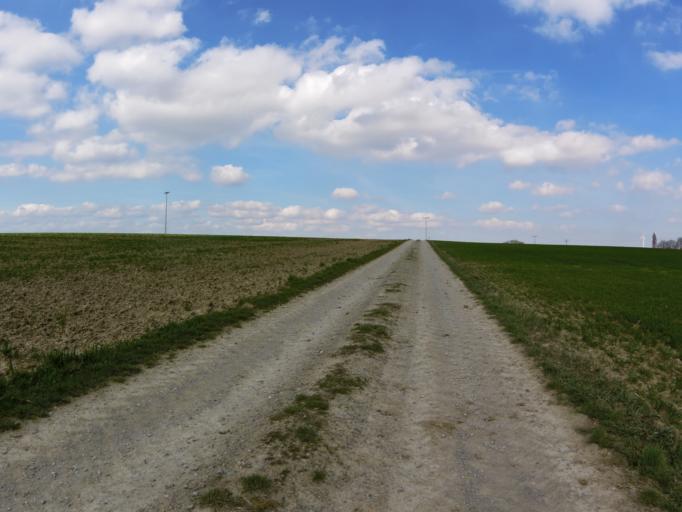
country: DE
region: Bavaria
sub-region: Regierungsbezirk Unterfranken
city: Biebelried
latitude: 49.7452
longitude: 10.0803
